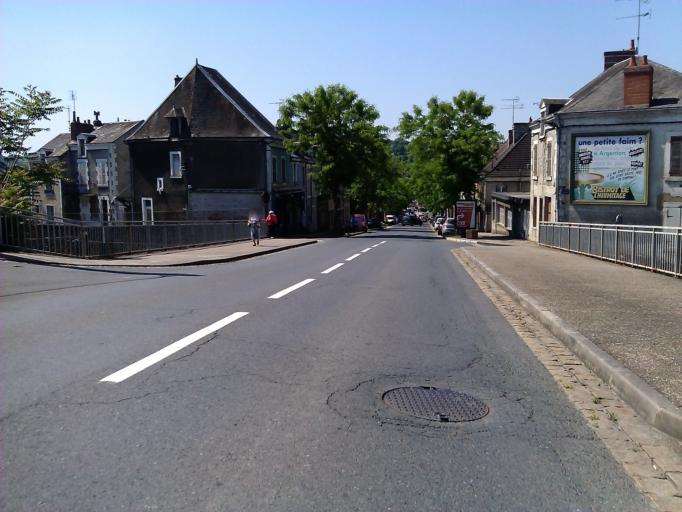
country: FR
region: Centre
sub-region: Departement de l'Indre
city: Argenton-sur-Creuse
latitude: 46.5910
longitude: 1.5204
